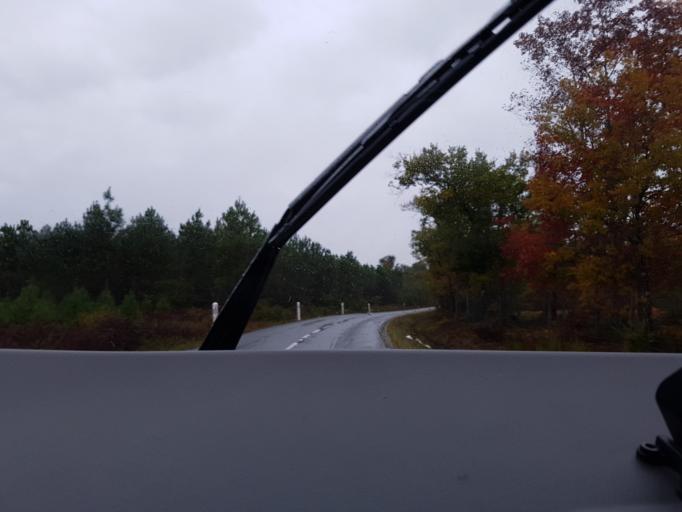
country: FR
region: Aquitaine
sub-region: Departement de la Gironde
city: Belin-Beliet
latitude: 44.4977
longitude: -0.7004
